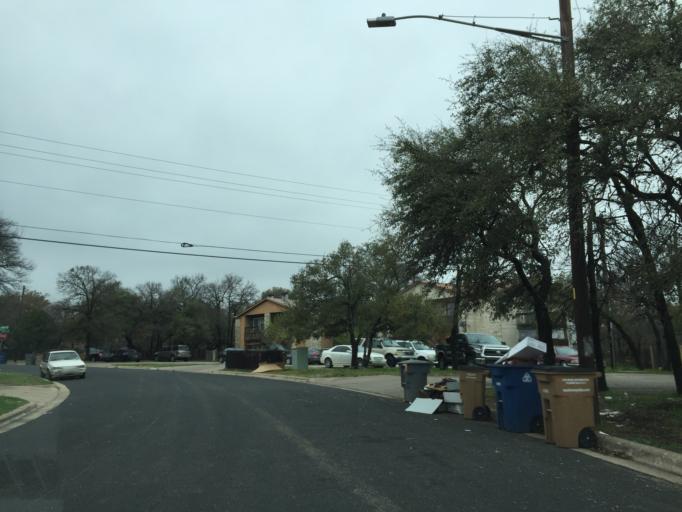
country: US
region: Texas
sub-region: Williamson County
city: Jollyville
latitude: 30.4139
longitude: -97.7299
